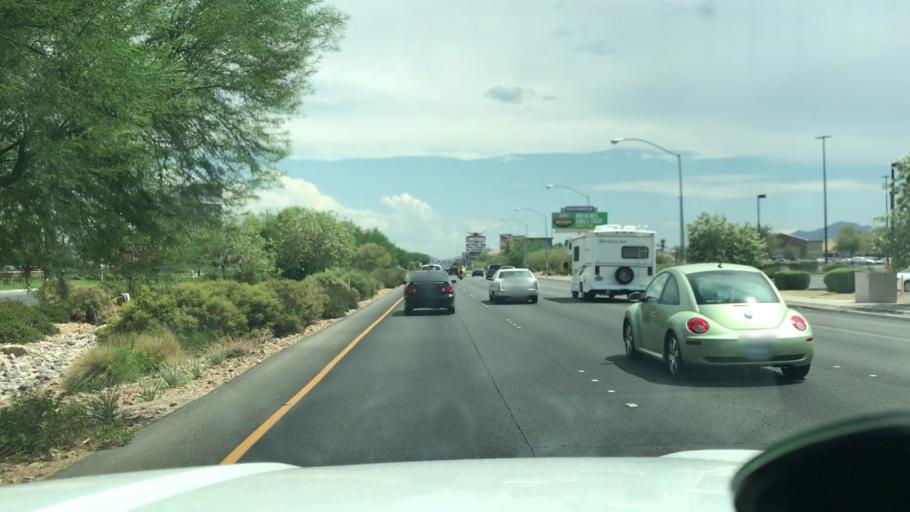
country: US
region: Nevada
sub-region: Clark County
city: Whitney
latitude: 36.1115
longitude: -115.0631
